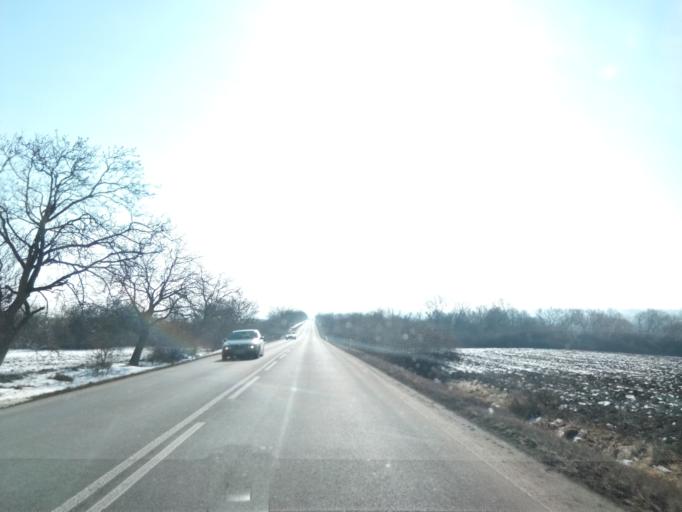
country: SK
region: Kosicky
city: Secovce
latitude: 48.7165
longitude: 21.6135
